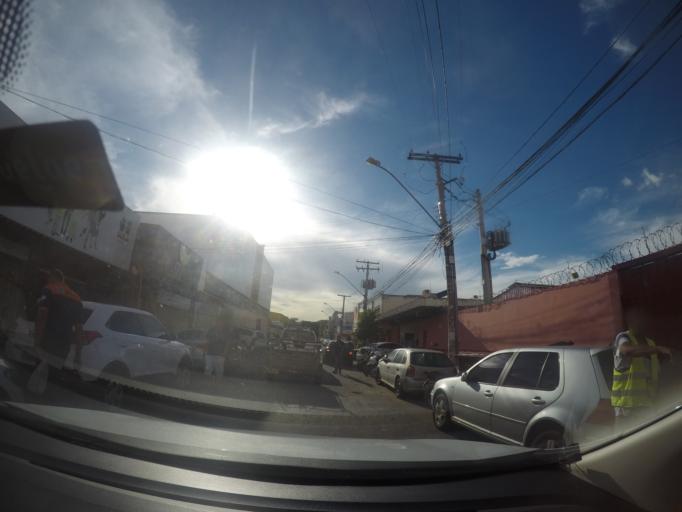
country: BR
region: Goias
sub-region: Goiania
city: Goiania
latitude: -16.6743
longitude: -49.2856
